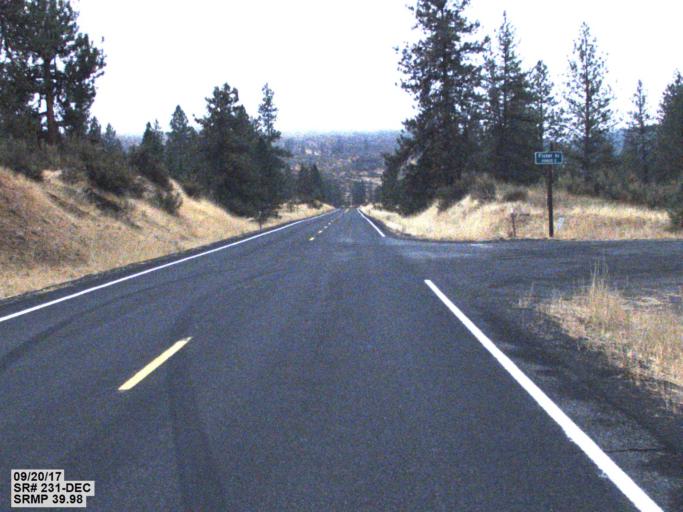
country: US
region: Washington
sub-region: Lincoln County
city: Davenport
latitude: 47.7889
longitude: -117.8899
